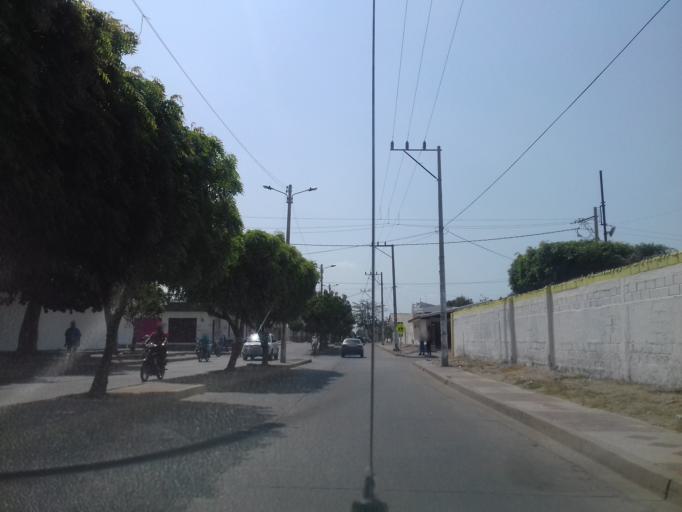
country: CO
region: La Guajira
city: Maicao
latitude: 11.3816
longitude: -72.2397
